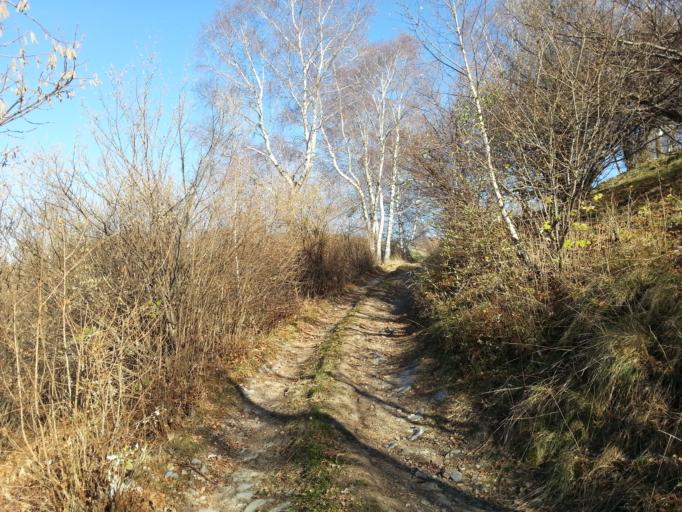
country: IT
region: Lombardy
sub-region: Provincia di Como
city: Maslianico
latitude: 45.8675
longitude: 9.0490
